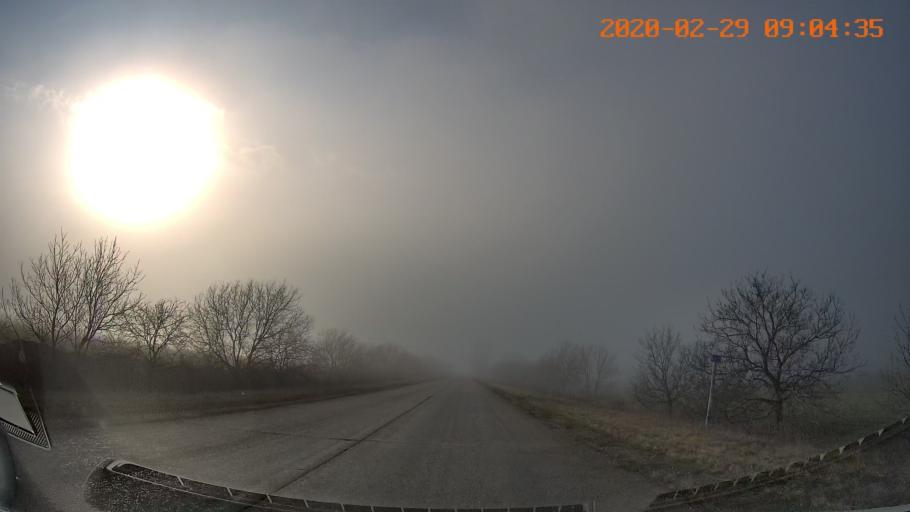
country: MD
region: Telenesti
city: Tiraspolul Nou
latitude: 46.9002
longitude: 29.7367
